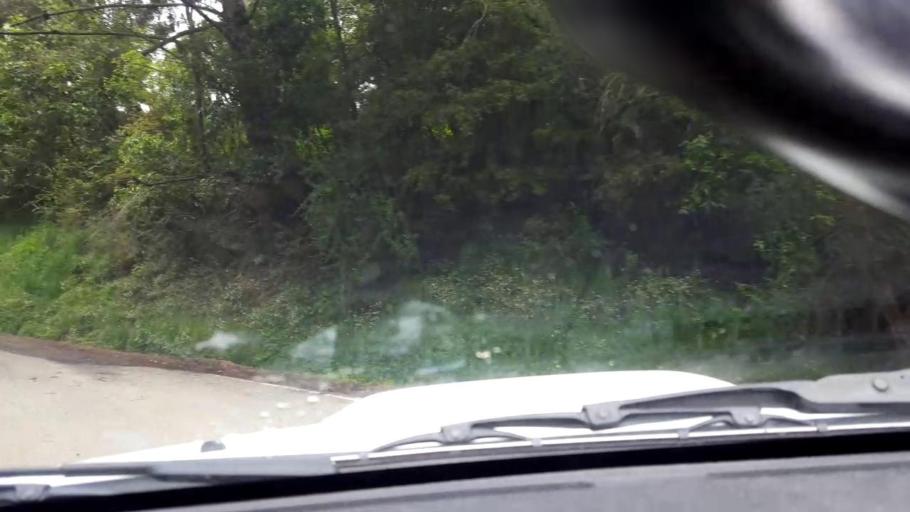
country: NZ
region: Gisborne
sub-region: Gisborne District
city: Gisborne
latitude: -38.3814
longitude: 177.6278
